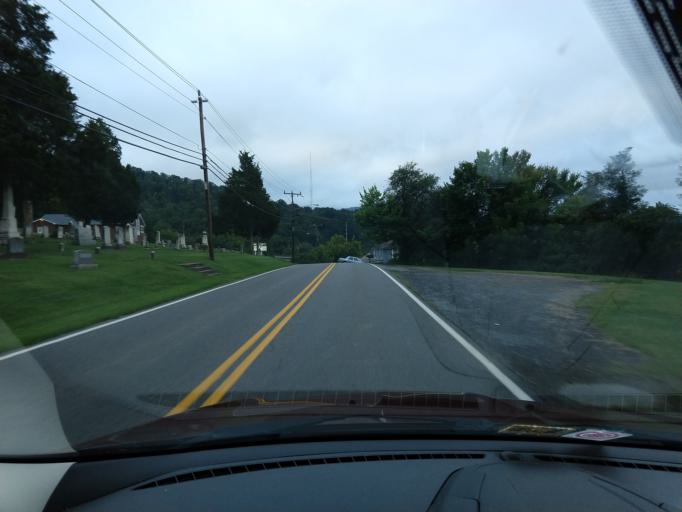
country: US
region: Virginia
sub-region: City of Covington
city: Fairlawn
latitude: 37.7744
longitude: -79.9861
